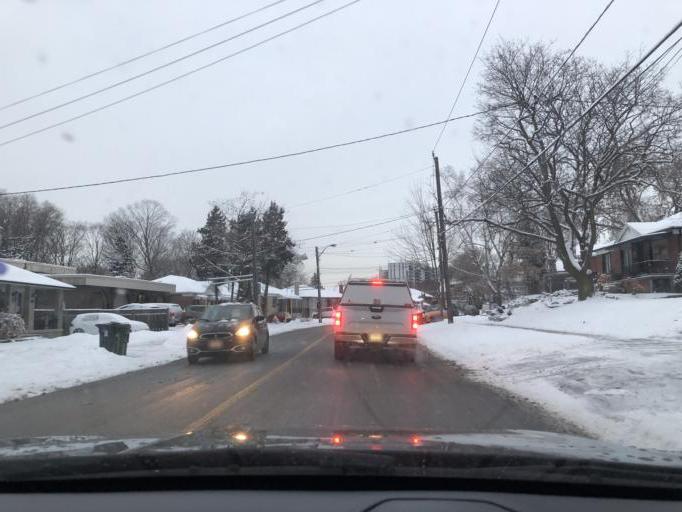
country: CA
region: Ontario
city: Toronto
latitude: 43.7018
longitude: -79.4856
